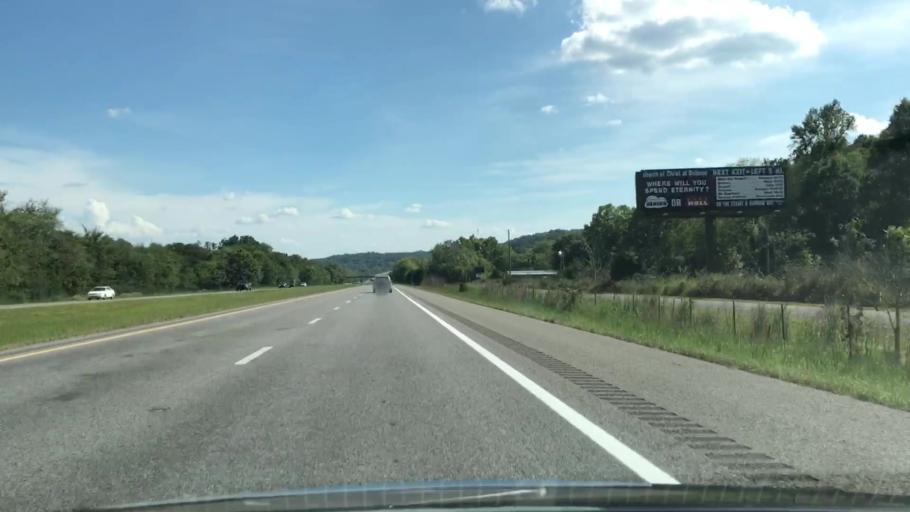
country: US
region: Alabama
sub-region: Limestone County
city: Ardmore
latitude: 35.1460
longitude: -86.8790
